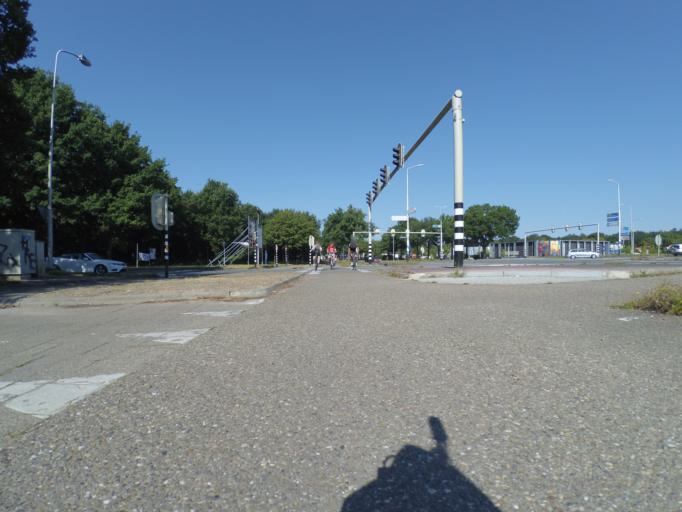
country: NL
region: Gelderland
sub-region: Gemeente Ede
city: Ede
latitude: 52.0506
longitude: 5.6764
